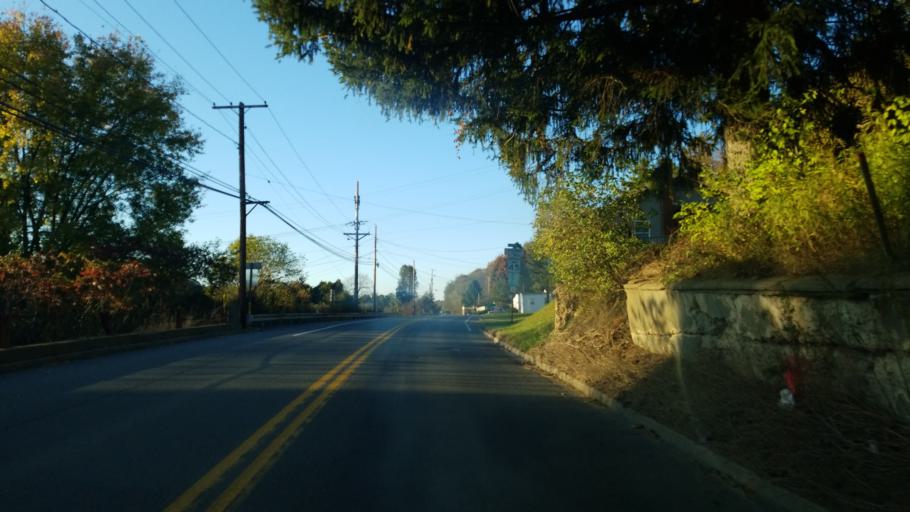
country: US
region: Pennsylvania
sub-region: Jefferson County
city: Punxsutawney
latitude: 40.9561
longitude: -78.9652
